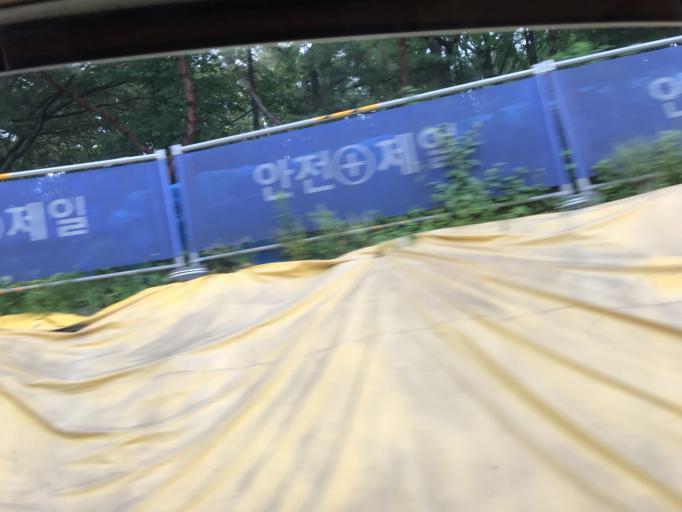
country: KR
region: Seoul
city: Seoul
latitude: 37.5778
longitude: 126.9925
